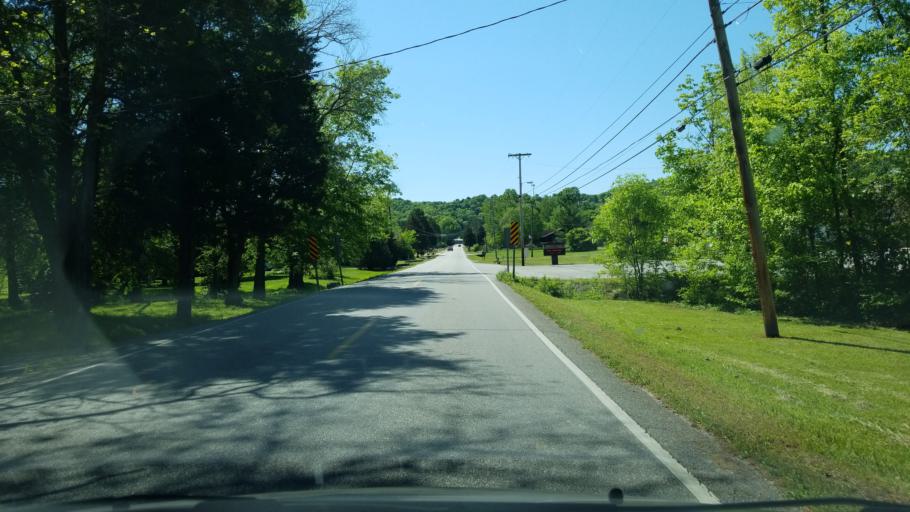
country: US
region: Tennessee
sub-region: Hamilton County
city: Middle Valley
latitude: 35.1778
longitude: -85.1803
